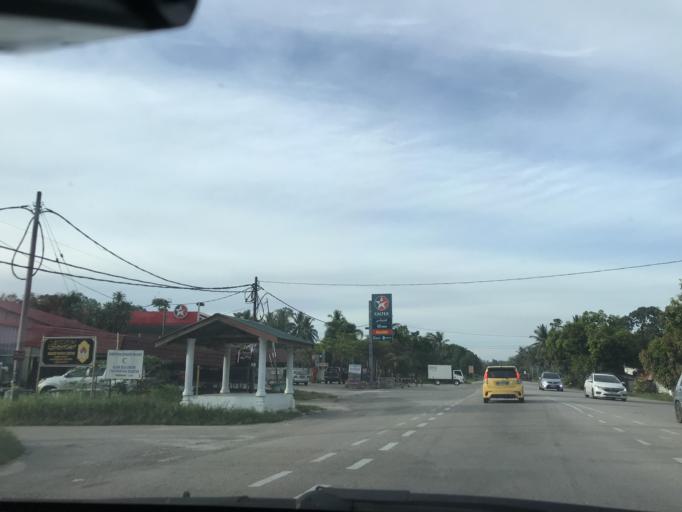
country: MY
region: Kelantan
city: Ketereh
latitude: 5.9679
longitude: 102.1935
